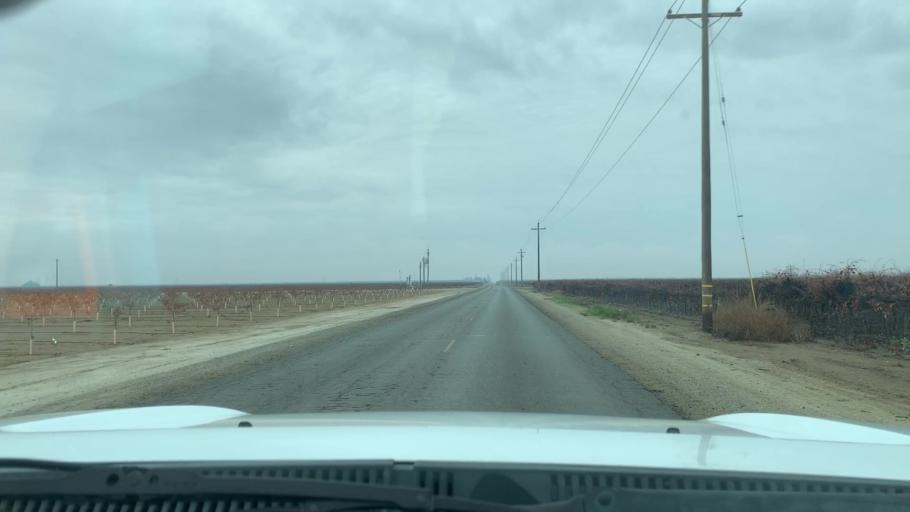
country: US
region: California
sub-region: Kern County
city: Delano
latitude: 35.7611
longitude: -119.3858
